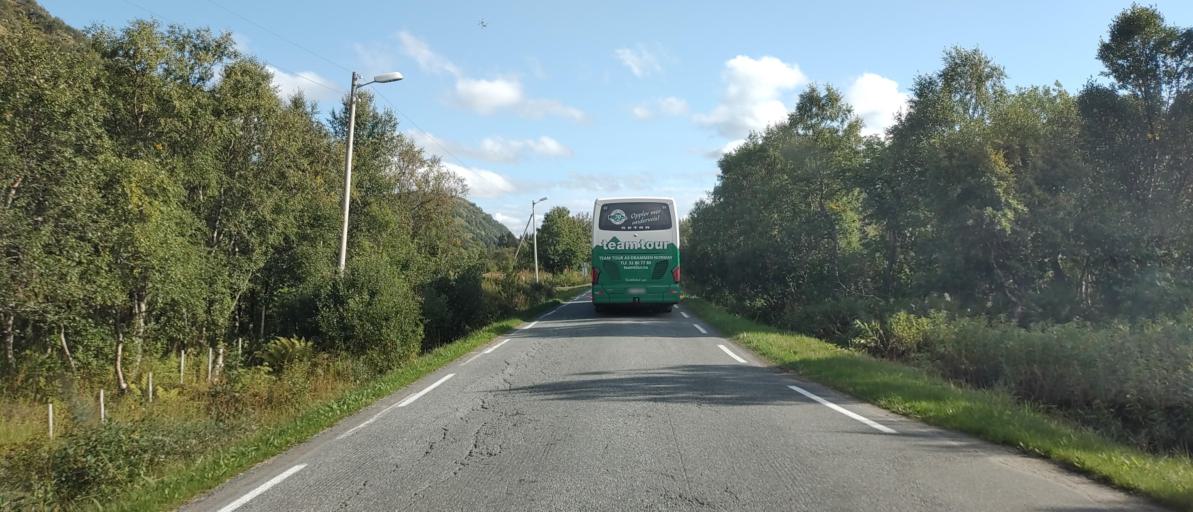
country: NO
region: Nordland
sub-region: Sortland
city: Sortland
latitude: 69.0356
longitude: 15.5236
